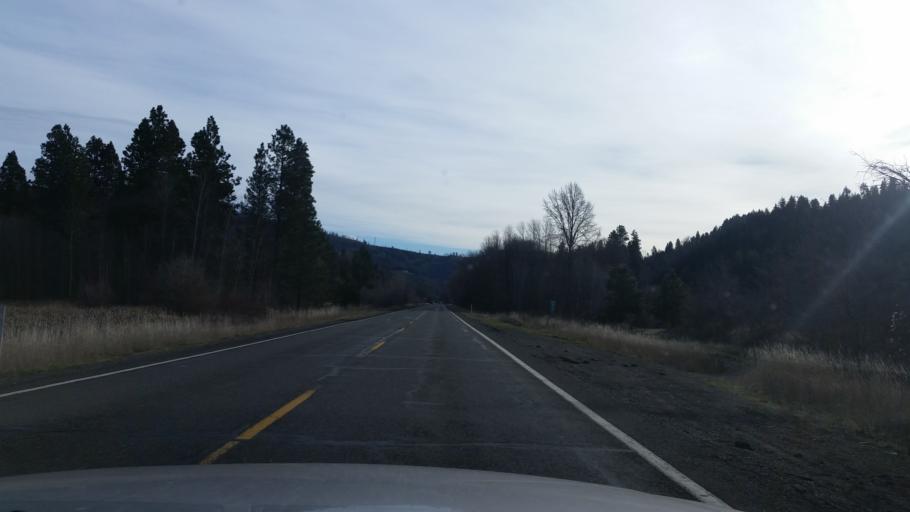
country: US
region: Washington
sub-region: Kittitas County
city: Cle Elum
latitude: 47.1711
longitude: -120.8433
